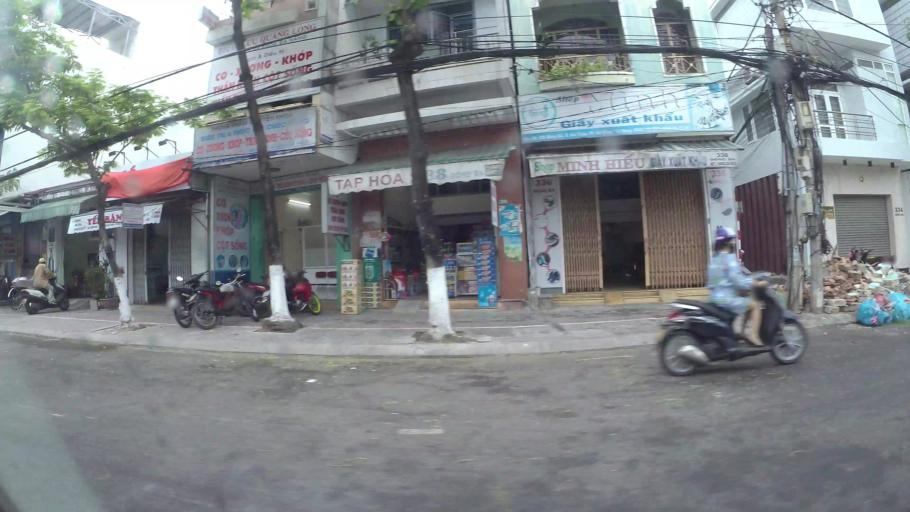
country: VN
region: Da Nang
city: Da Nang
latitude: 16.0749
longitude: 108.2145
